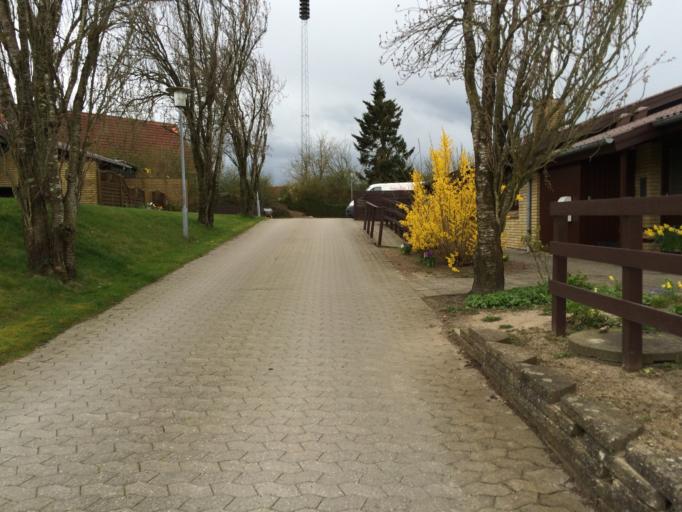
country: DK
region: South Denmark
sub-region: Odense Kommune
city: Bellinge
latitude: 55.2703
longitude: 10.3179
